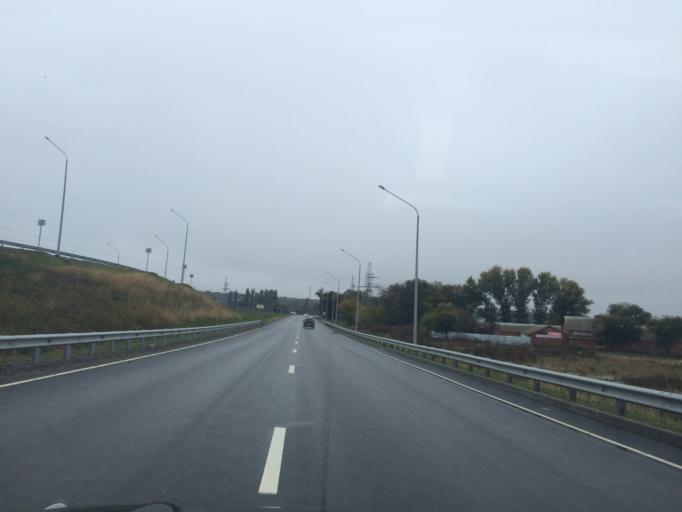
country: RU
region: Rostov
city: Kuleshovka
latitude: 47.0864
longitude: 39.4917
